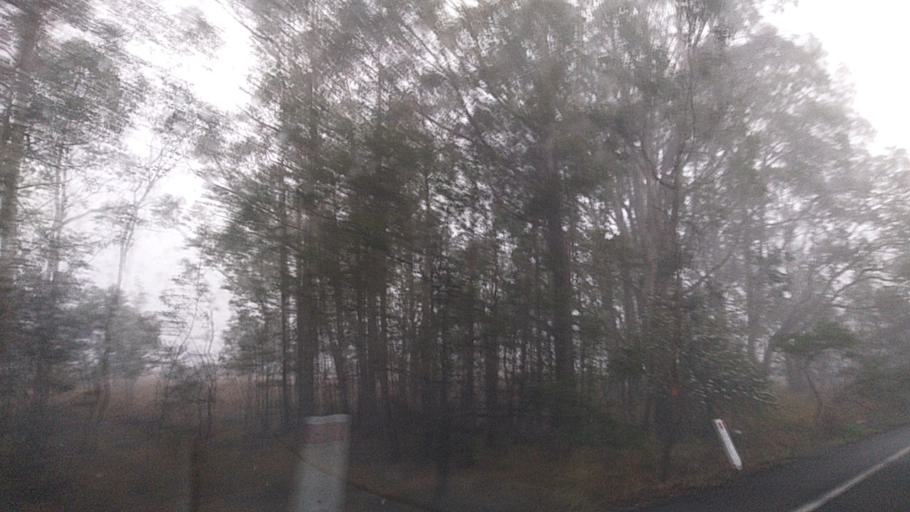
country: AU
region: New South Wales
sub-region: Wollondilly
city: Douglas Park
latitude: -34.2646
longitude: 150.7175
